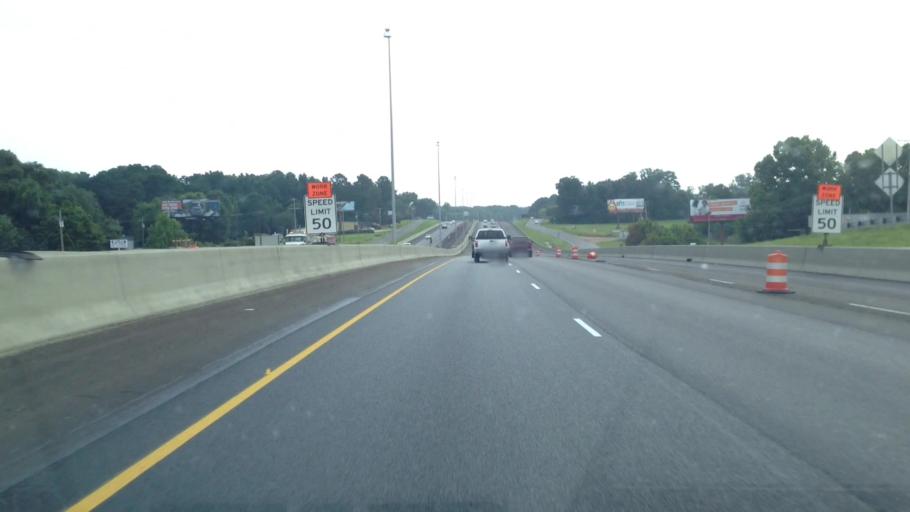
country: US
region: Mississippi
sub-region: Hinds County
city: Byram
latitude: 32.1931
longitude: -90.2518
